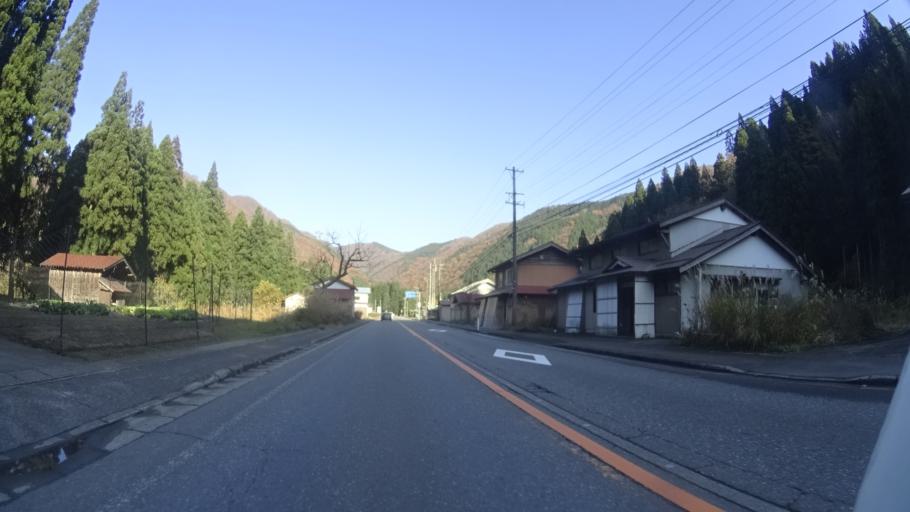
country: JP
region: Fukui
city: Ono
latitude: 35.9204
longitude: 136.6372
